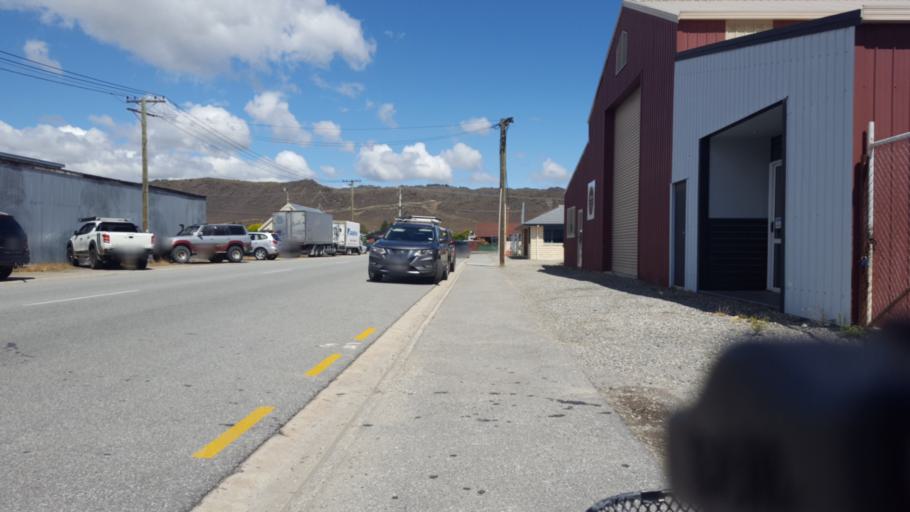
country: NZ
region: Otago
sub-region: Queenstown-Lakes District
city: Wanaka
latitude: -45.2456
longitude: 169.3935
